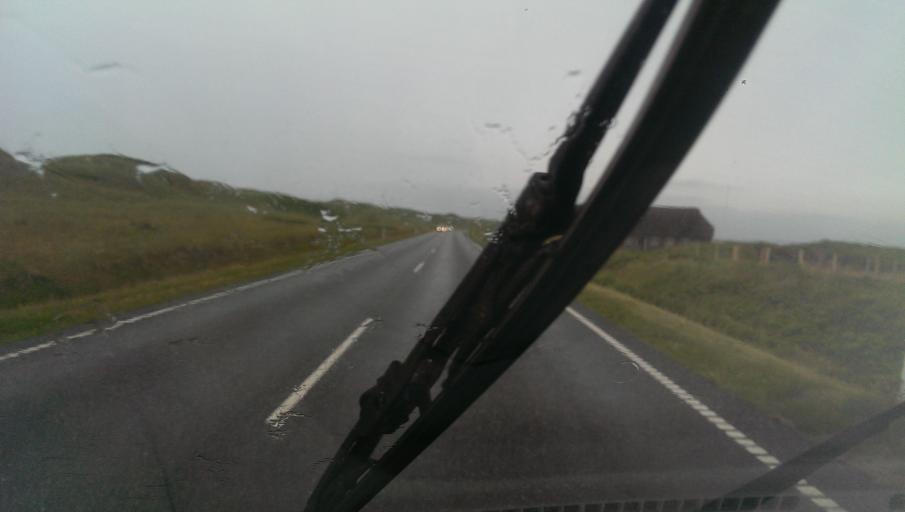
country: DK
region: Central Jutland
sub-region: Ringkobing-Skjern Kommune
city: Ringkobing
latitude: 56.1825
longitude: 8.1273
